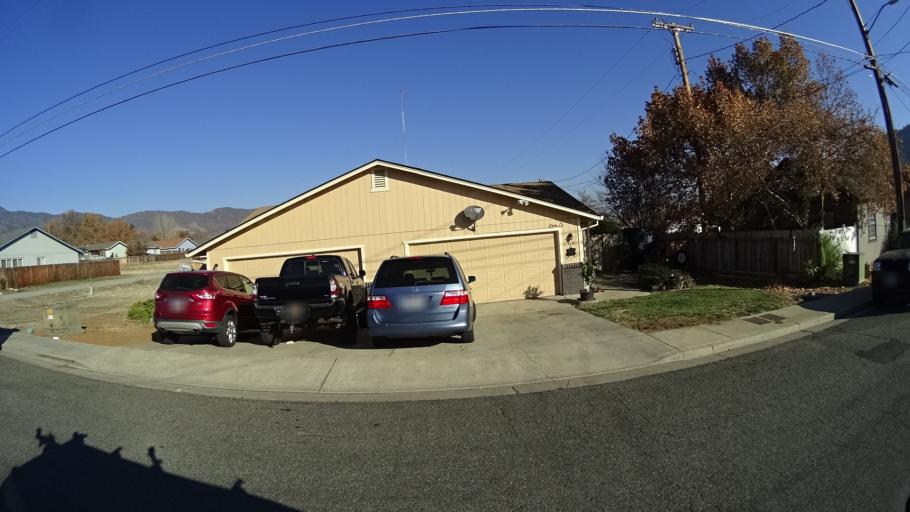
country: US
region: California
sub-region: Siskiyou County
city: Yreka
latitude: 41.7208
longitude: -122.6436
